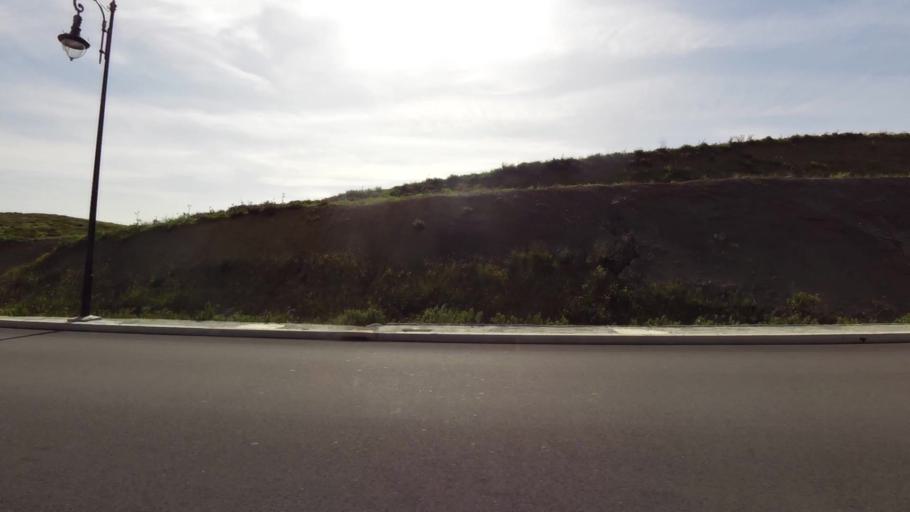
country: MA
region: Tanger-Tetouan
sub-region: Tanger-Assilah
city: Tangier
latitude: 35.7124
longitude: -5.7770
